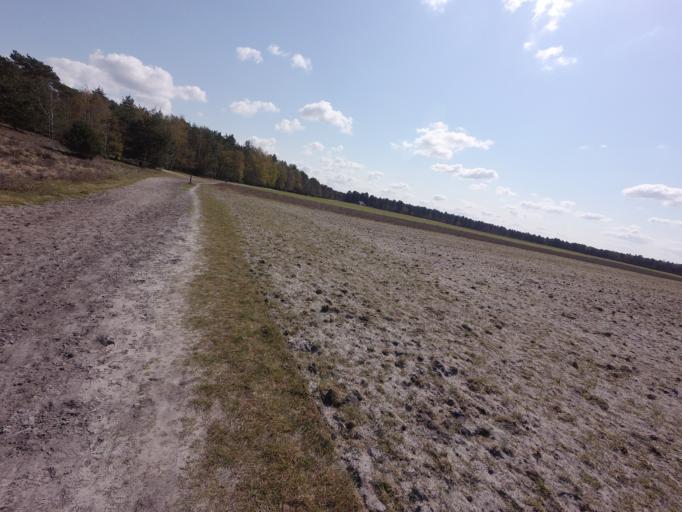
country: NL
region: Limburg
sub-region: Gemeente Bergen
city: Wellerlooi
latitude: 51.5941
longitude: 6.1067
